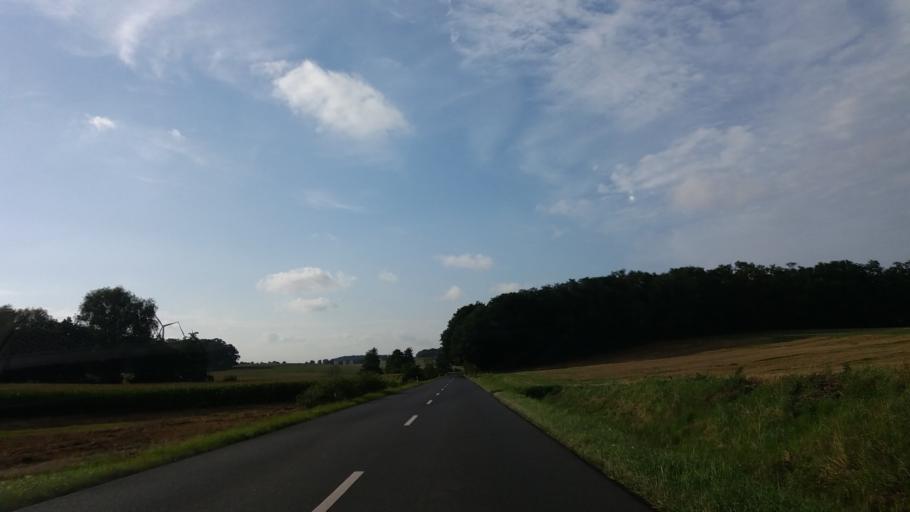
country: PL
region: Lower Silesian Voivodeship
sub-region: Powiat legnicki
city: Legnickie Pole
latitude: 51.1584
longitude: 16.3401
